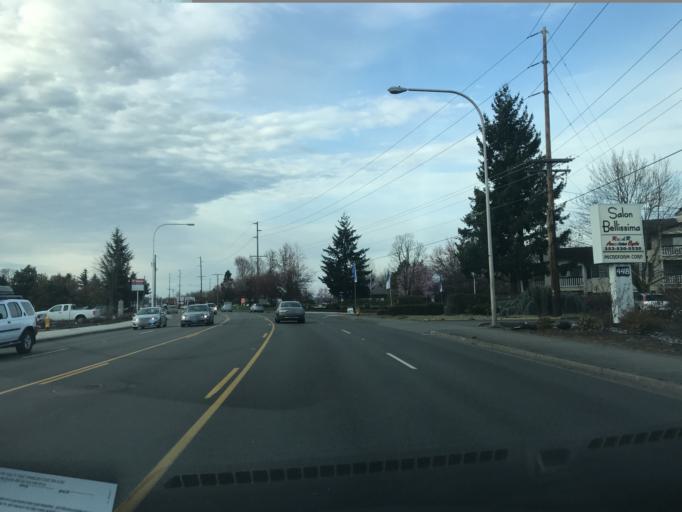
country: US
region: Washington
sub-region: King County
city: Kent
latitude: 47.3467
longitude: -122.2226
